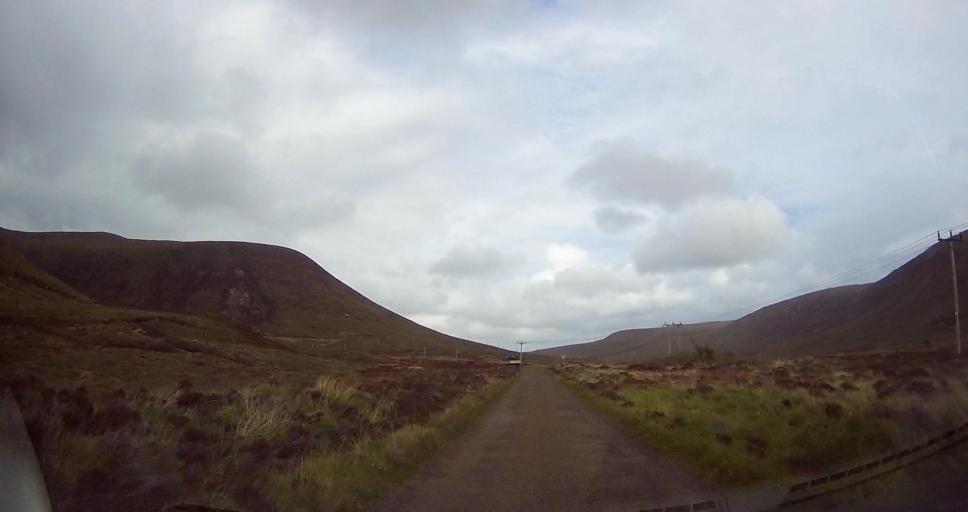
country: GB
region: Scotland
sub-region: Orkney Islands
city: Stromness
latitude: 58.8842
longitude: -3.3349
